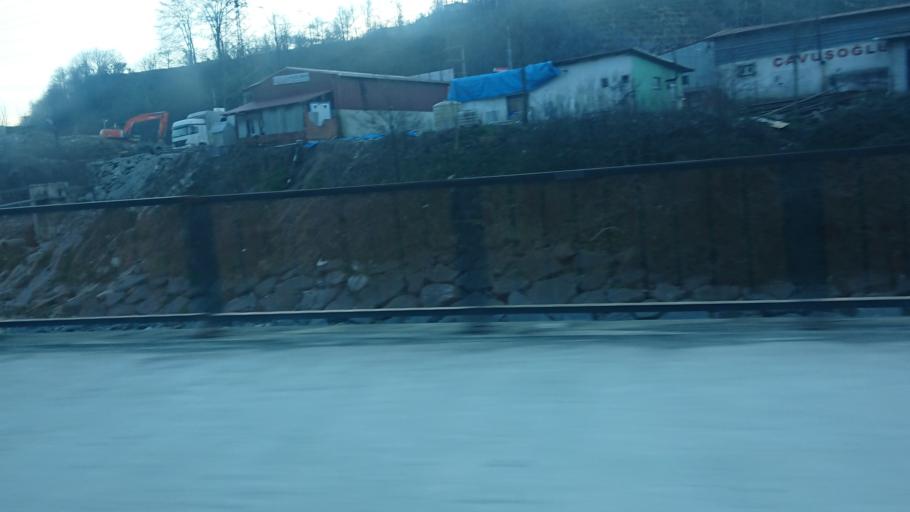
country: TR
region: Rize
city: Gundogdu
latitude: 41.0309
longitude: 40.5834
